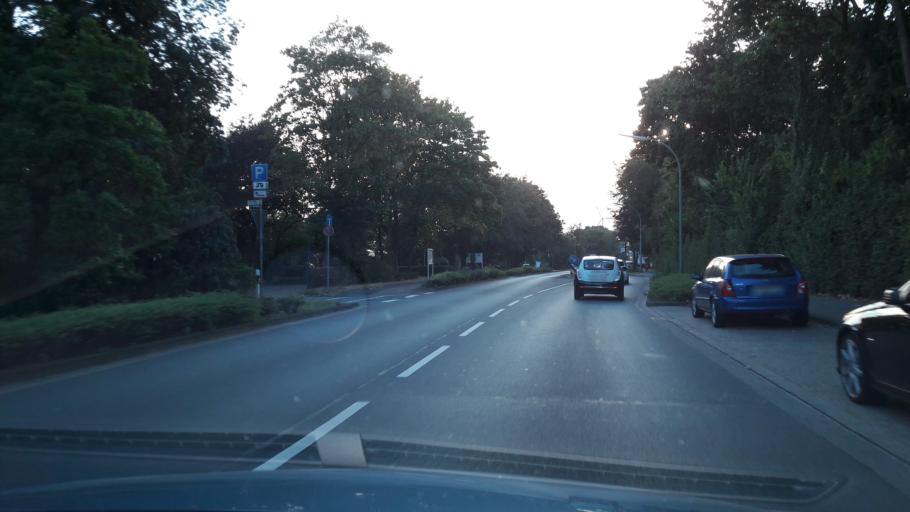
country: DE
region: North Rhine-Westphalia
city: Sendenhorst
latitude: 51.8432
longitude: 7.8189
